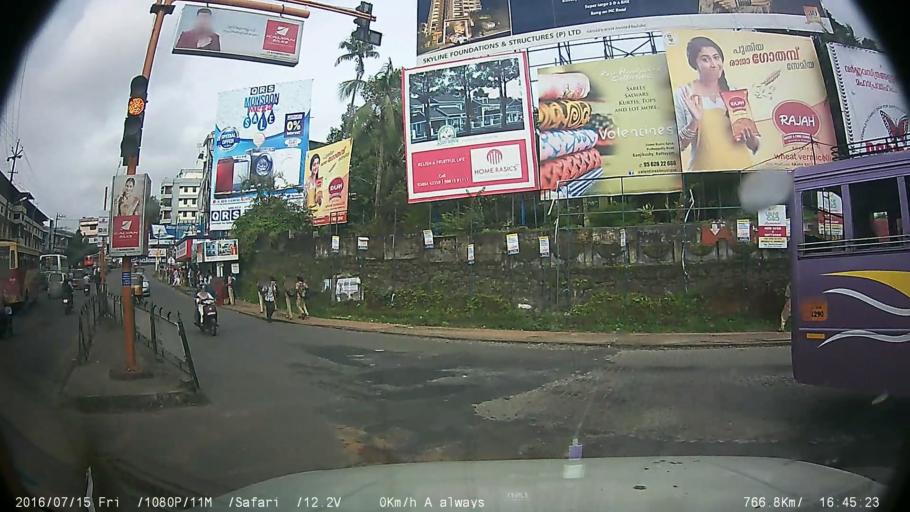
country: IN
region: Kerala
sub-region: Kottayam
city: Kottayam
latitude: 9.5916
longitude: 76.5310
